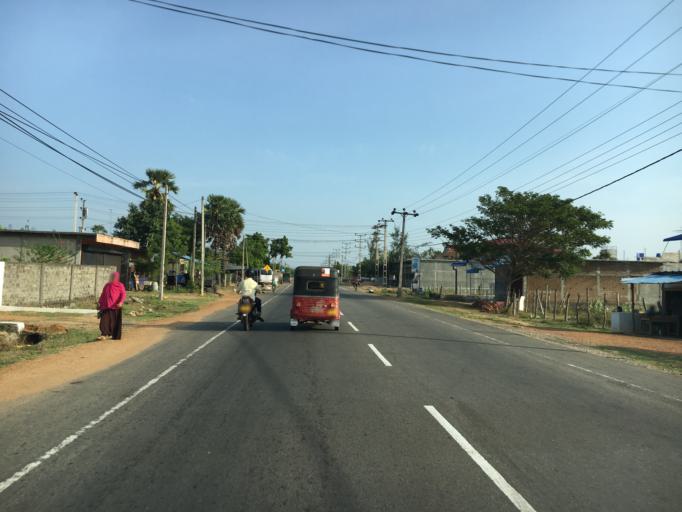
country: LK
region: Eastern Province
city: Eravur Town
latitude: 7.9306
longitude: 81.5121
